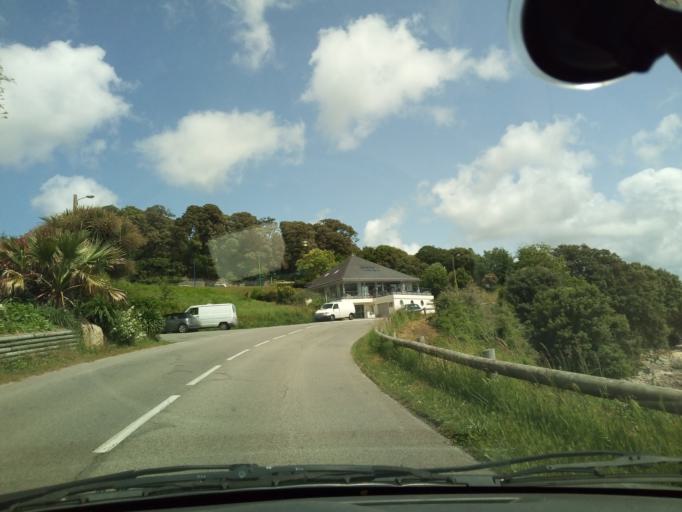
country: FR
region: Brittany
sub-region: Departement du Finistere
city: Audierne
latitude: 48.0171
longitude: -4.5383
